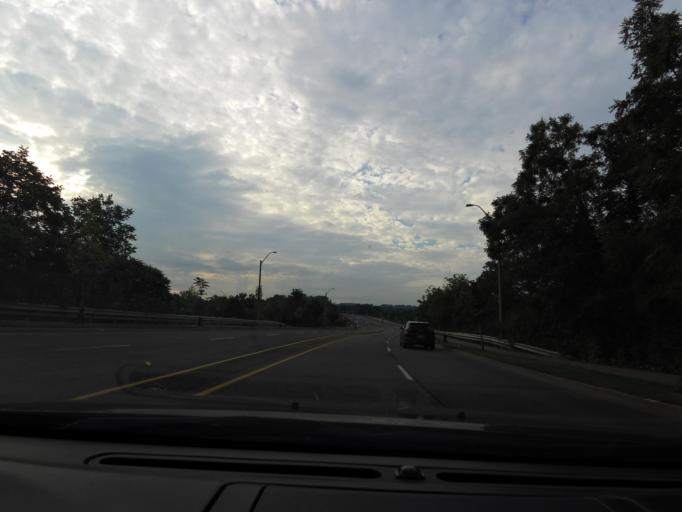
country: CA
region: Ontario
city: Hamilton
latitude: 43.2285
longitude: -79.7933
